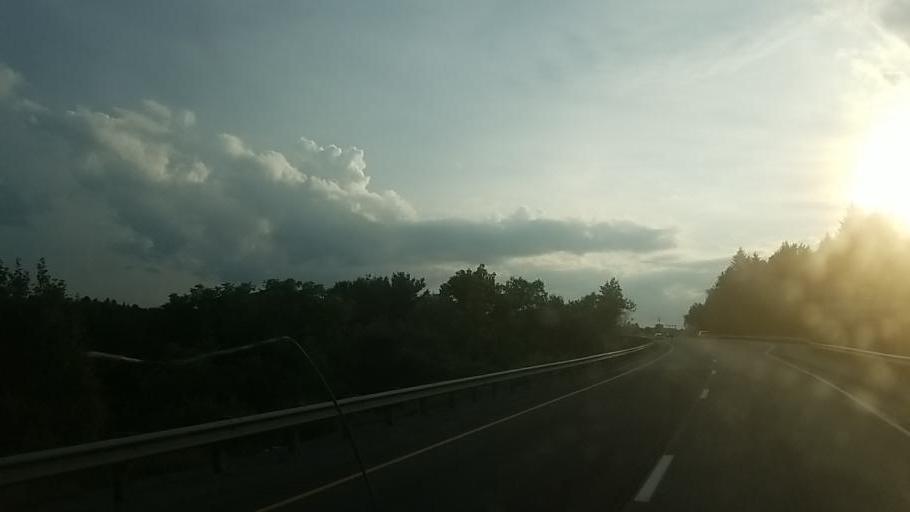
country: US
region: Pennsylvania
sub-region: Clearfield County
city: Troy
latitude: 40.9898
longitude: -78.1614
